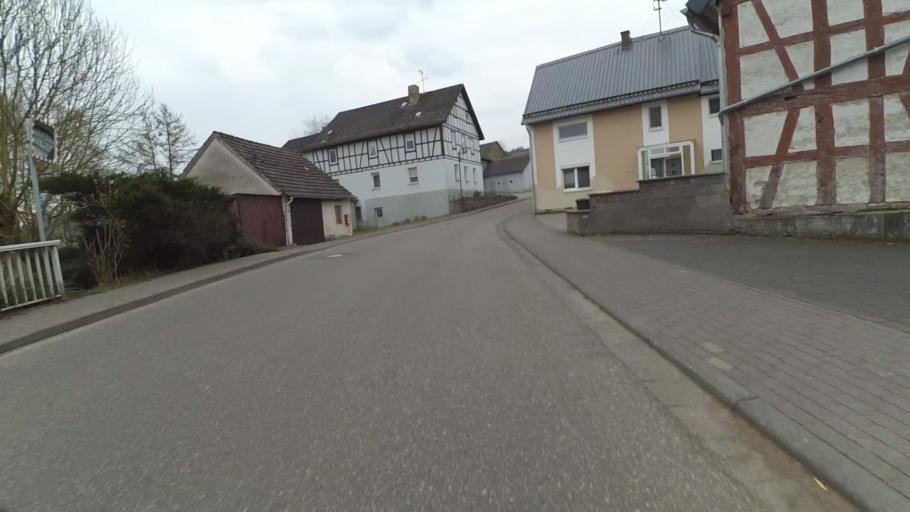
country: DE
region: Rheinland-Pfalz
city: Quirnbach
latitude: 50.5189
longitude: 7.7955
